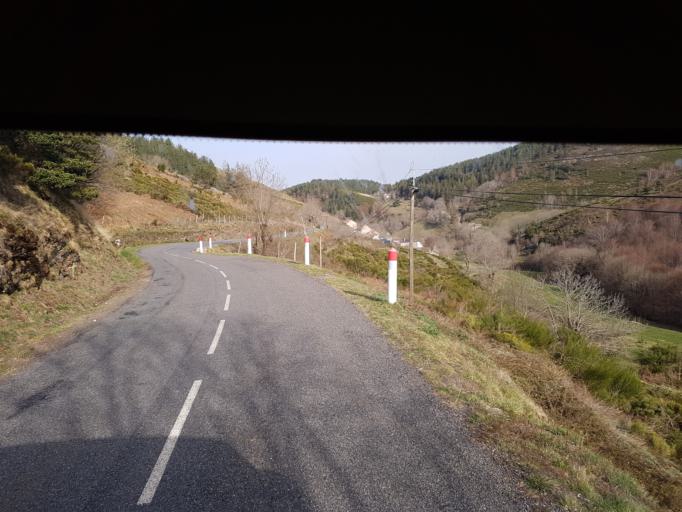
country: FR
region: Languedoc-Roussillon
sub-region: Departement du Gard
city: Branoux-les-Taillades
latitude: 44.3243
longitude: 3.8245
